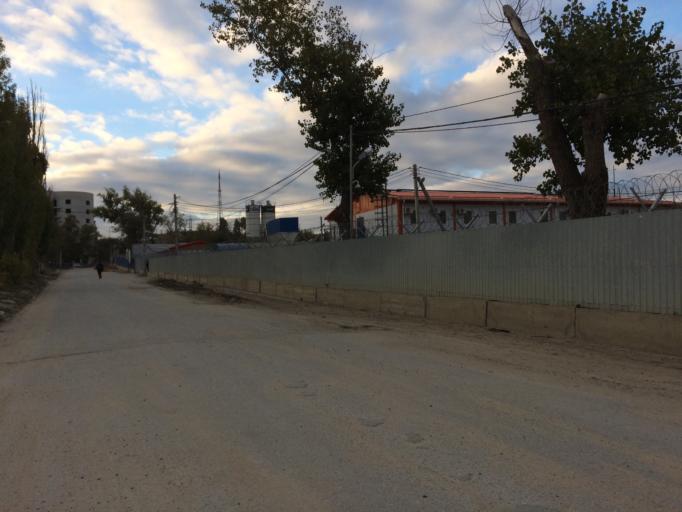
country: RU
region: Volgograd
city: Krasnoslobodsk
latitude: 48.7335
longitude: 44.5452
